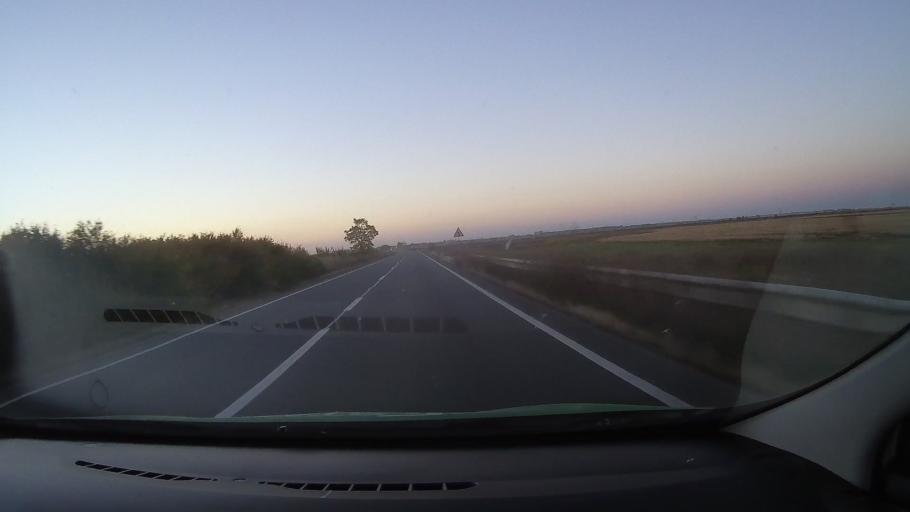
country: RO
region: Bihor
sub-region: Comuna Tarcea
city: Tarcea
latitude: 47.4416
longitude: 22.1916
